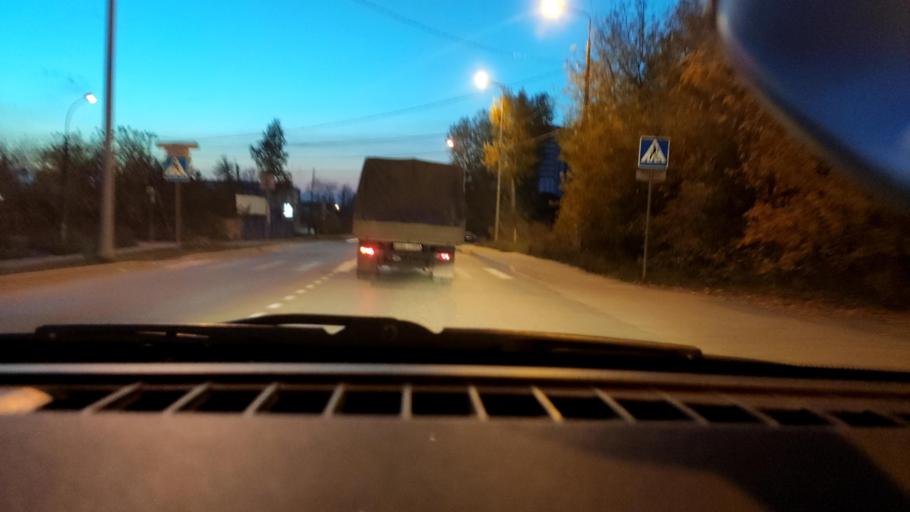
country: RU
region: Perm
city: Kondratovo
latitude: 57.9623
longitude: 56.1603
